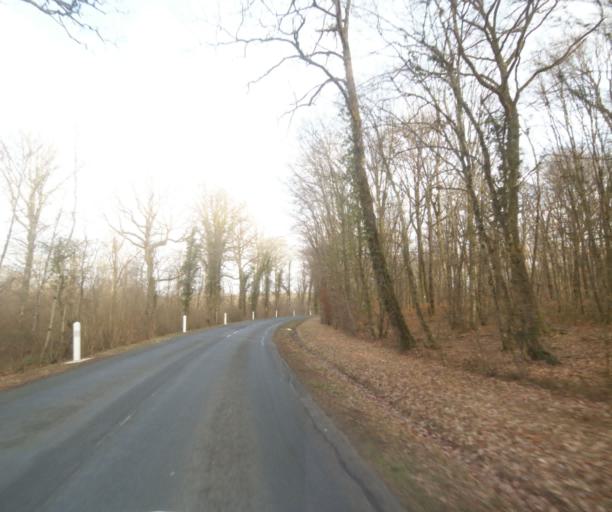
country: FR
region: Champagne-Ardenne
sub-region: Departement de la Marne
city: Sermaize-les-Bains
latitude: 48.7529
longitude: 4.9005
